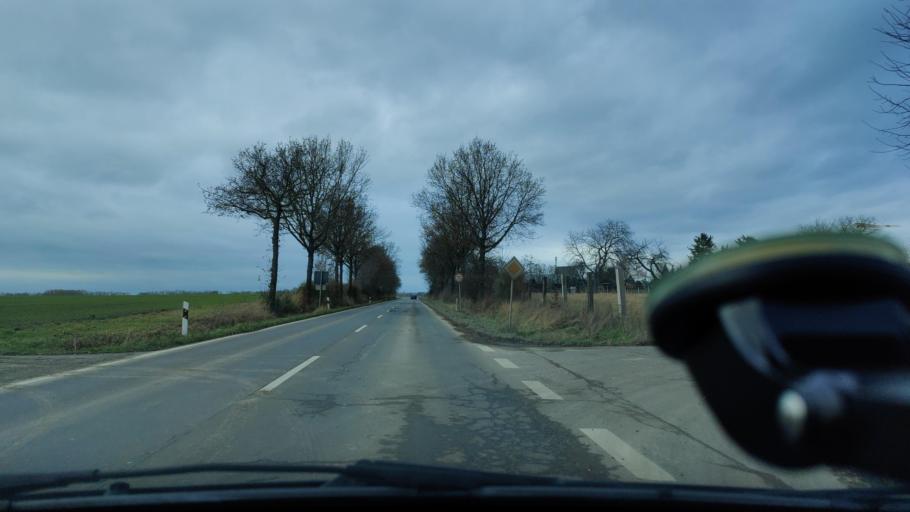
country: DE
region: North Rhine-Westphalia
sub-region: Regierungsbezirk Koln
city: Titz
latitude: 51.0029
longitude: 6.4208
